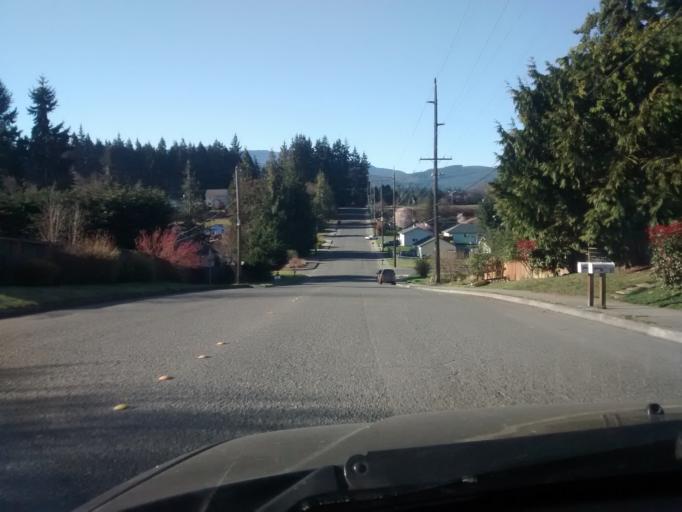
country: US
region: Washington
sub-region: Clallam County
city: Port Angeles
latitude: 48.1208
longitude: -123.4730
